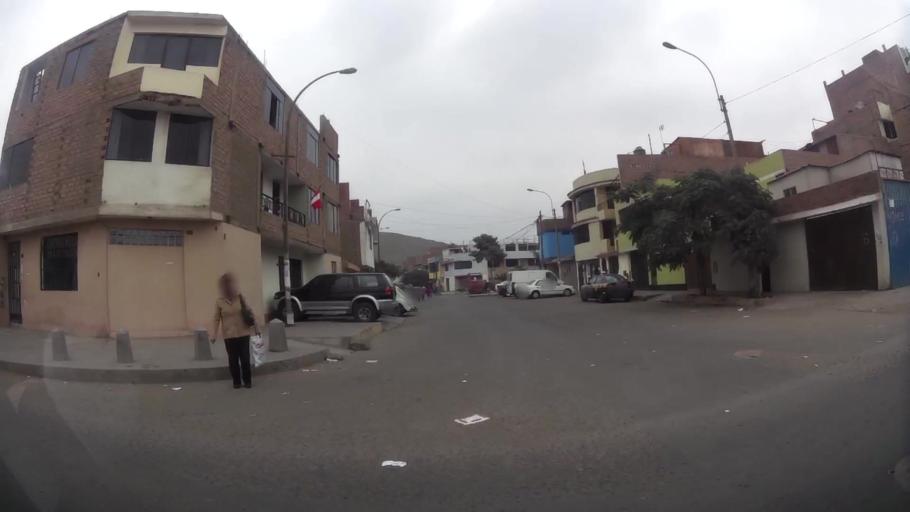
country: PE
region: Lima
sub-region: Lima
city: Independencia
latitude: -11.9404
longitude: -77.0863
